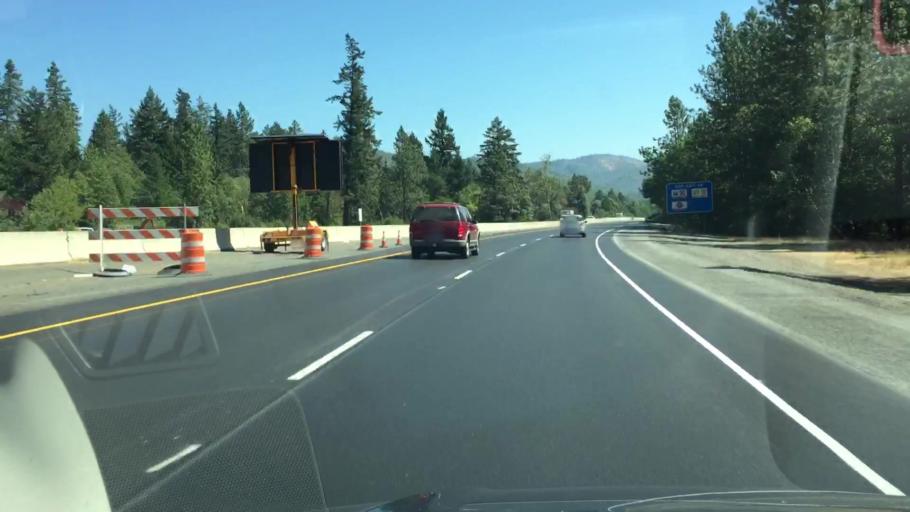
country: US
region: Oregon
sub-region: Jackson County
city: Rogue River
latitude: 42.4312
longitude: -123.1866
